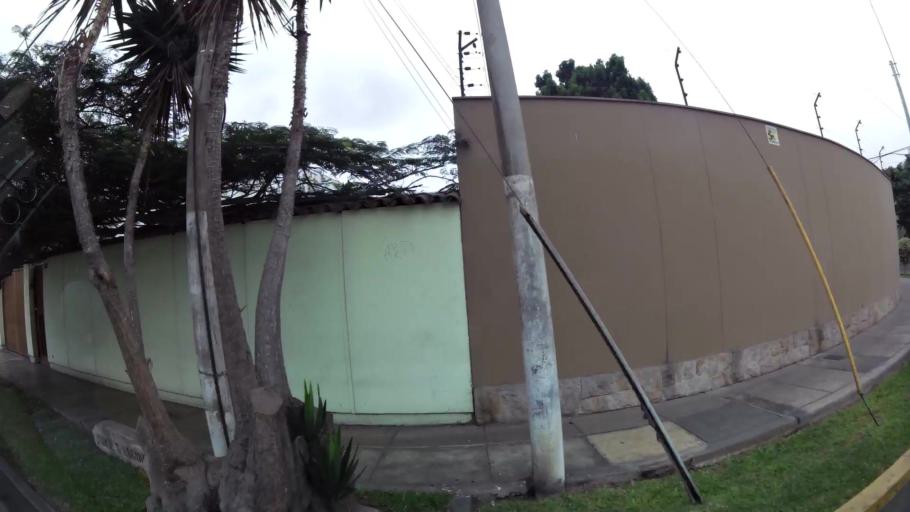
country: PE
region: Lima
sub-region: Lima
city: Surco
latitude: -12.1233
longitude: -77.0110
